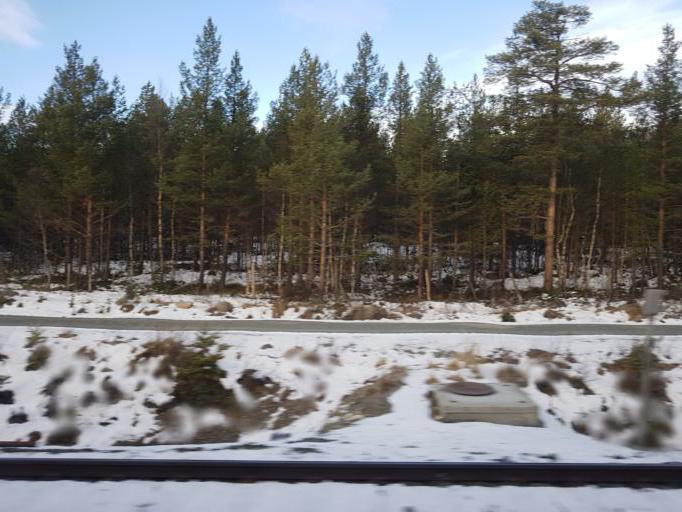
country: NO
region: Sor-Trondelag
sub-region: Oppdal
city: Oppdal
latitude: 62.6316
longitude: 9.7906
